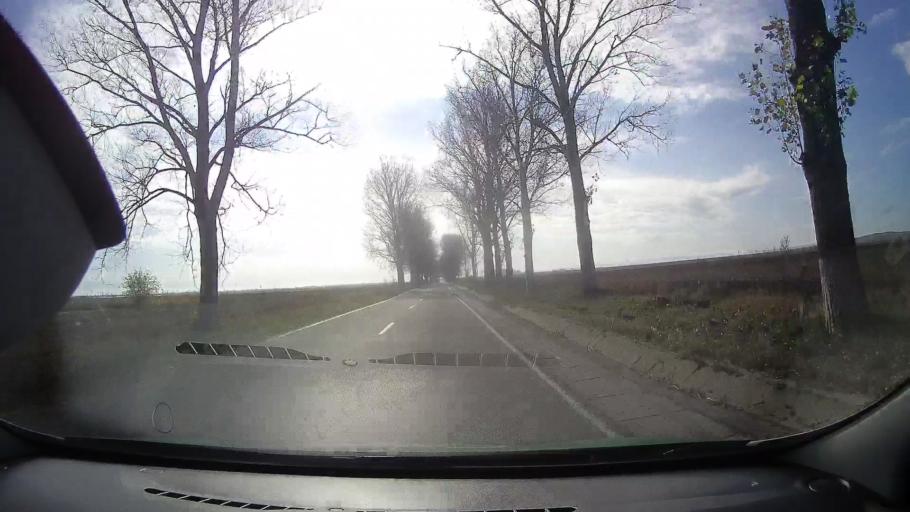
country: RO
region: Tulcea
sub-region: Comuna Valea Nucarilor
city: Agighiol
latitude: 45.0062
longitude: 28.8851
